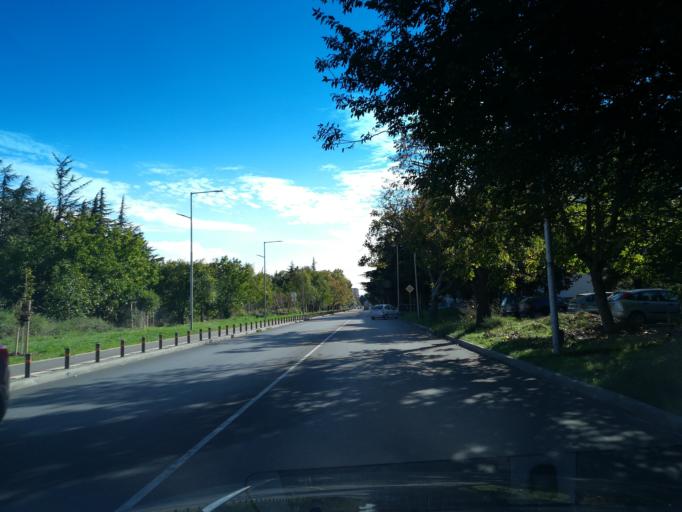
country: BG
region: Stara Zagora
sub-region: Obshtina Stara Zagora
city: Stara Zagora
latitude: 42.4378
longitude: 25.6359
